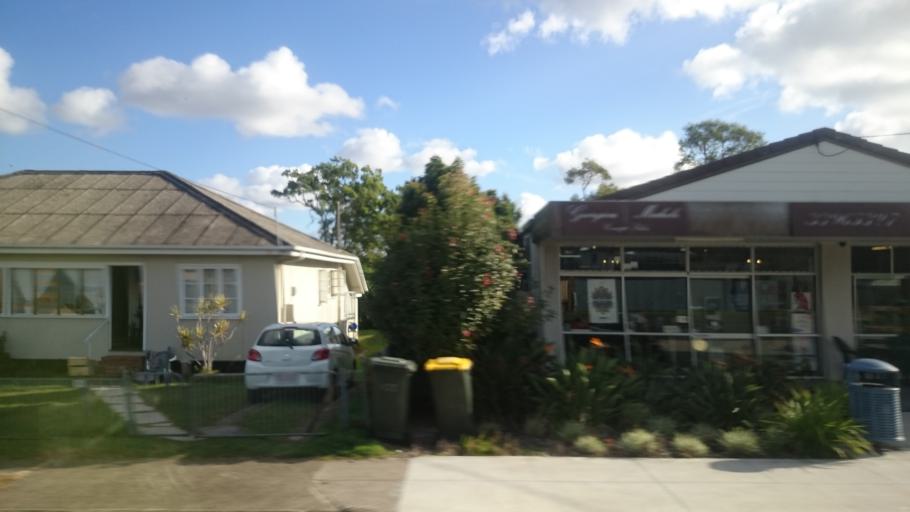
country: AU
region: Queensland
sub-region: Brisbane
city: Manly West
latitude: -27.4630
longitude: 153.1802
